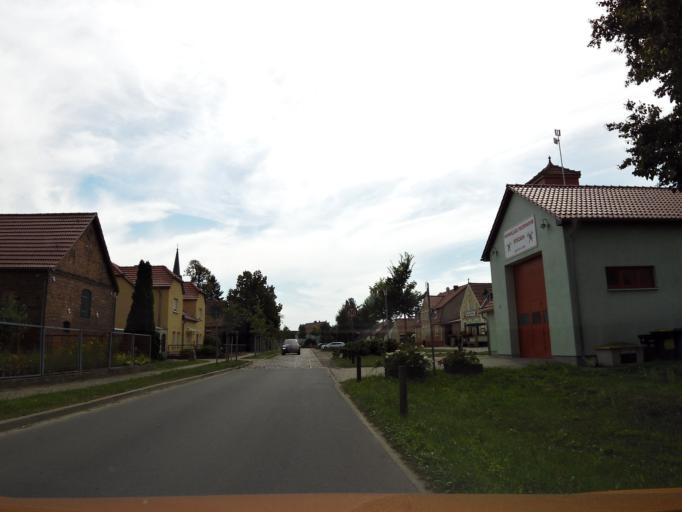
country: DE
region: Brandenburg
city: Michendorf
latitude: 52.2458
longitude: 13.0803
